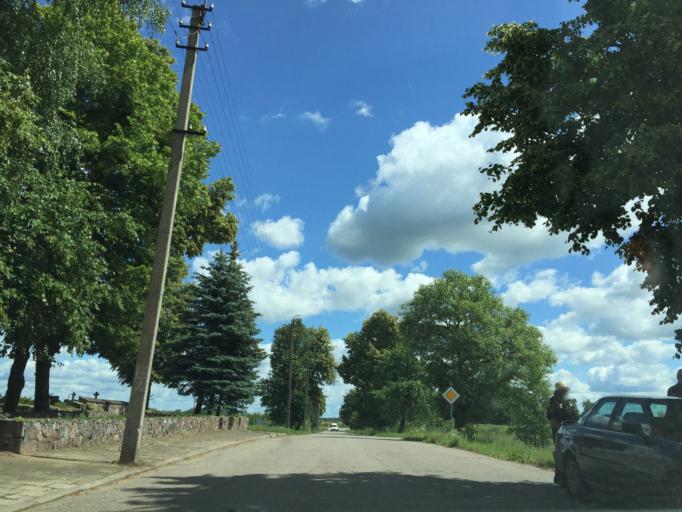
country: LT
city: Ramygala
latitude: 55.5153
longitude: 24.3073
